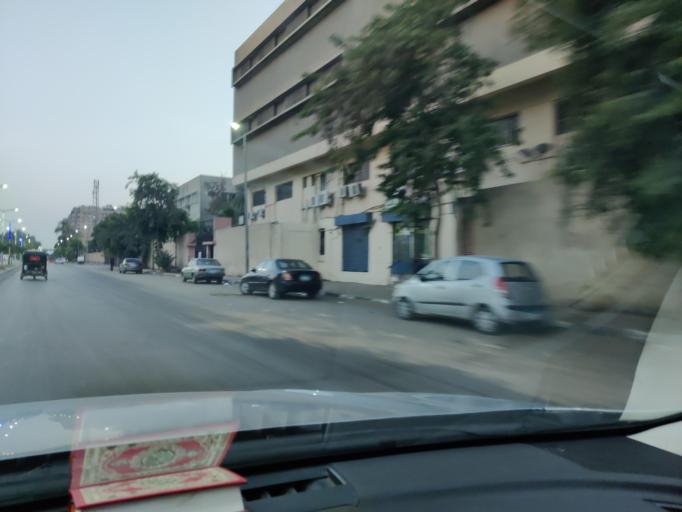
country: EG
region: Muhafazat al Qahirah
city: Cairo
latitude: 30.1063
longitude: 31.3027
